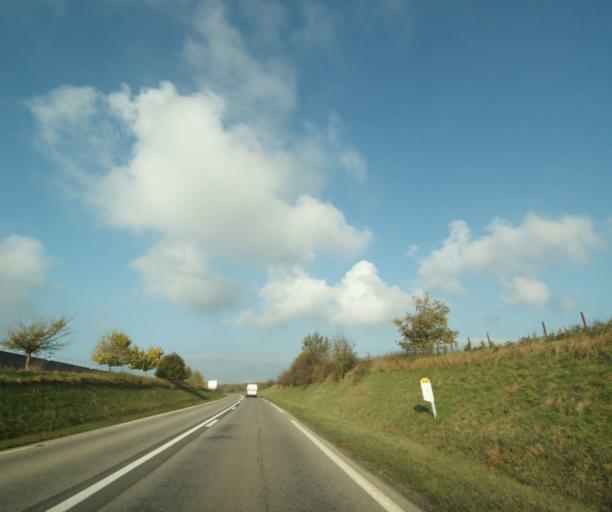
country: FR
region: Lorraine
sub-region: Departement de Meurthe-et-Moselle
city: Briey
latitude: 49.2564
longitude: 5.9467
